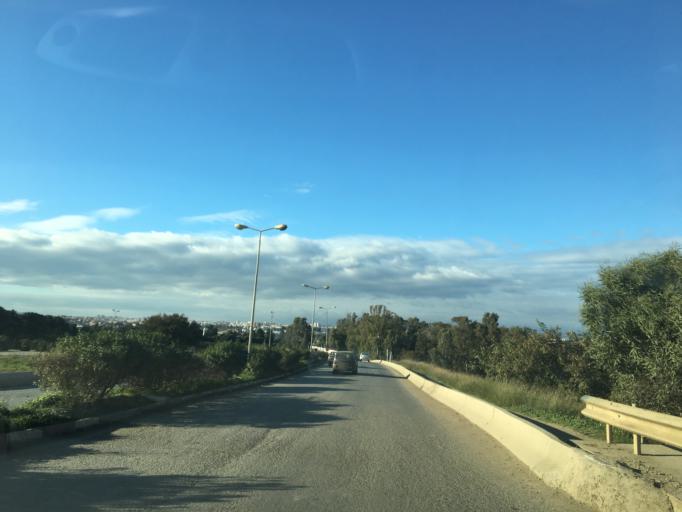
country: DZ
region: Tipaza
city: Baraki
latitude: 36.6871
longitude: 3.1141
